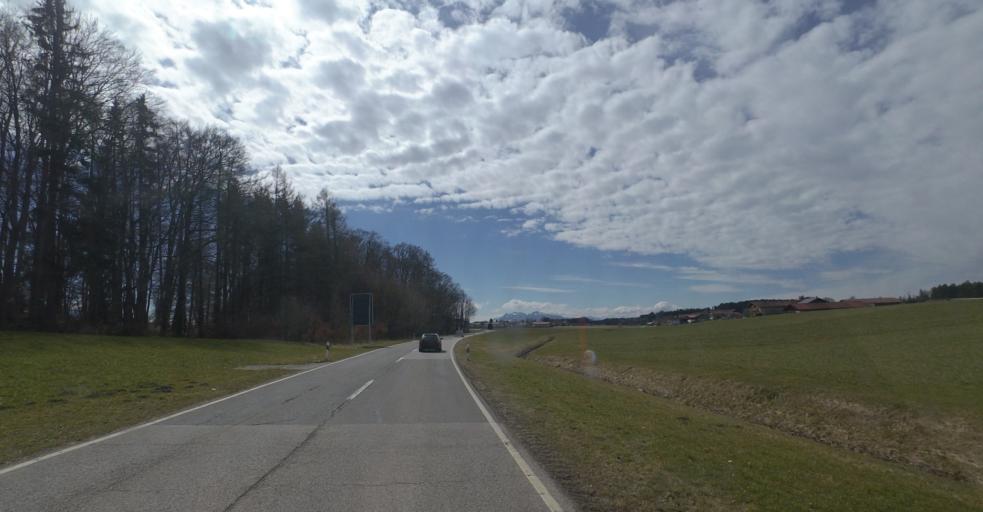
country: DE
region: Bavaria
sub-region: Upper Bavaria
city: Gstadt am Chiemsee
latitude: 47.9222
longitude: 12.4425
